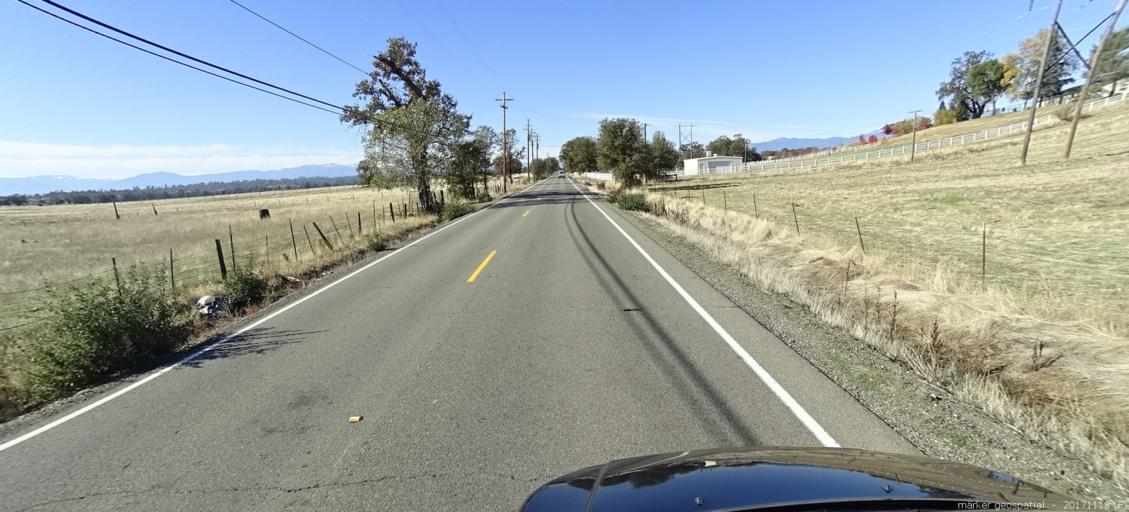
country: US
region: California
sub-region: Shasta County
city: Anderson
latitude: 40.3887
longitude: -122.3939
